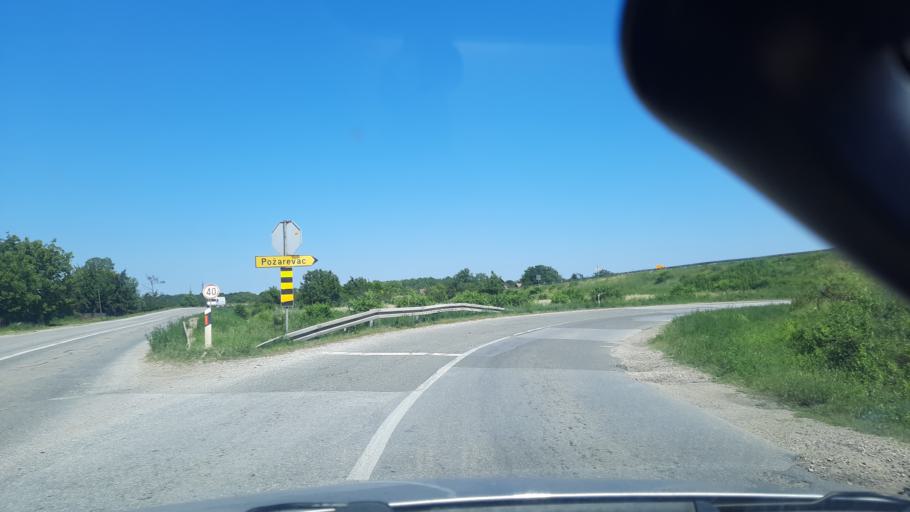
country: RS
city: Lugavcina
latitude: 44.5893
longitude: 21.0004
